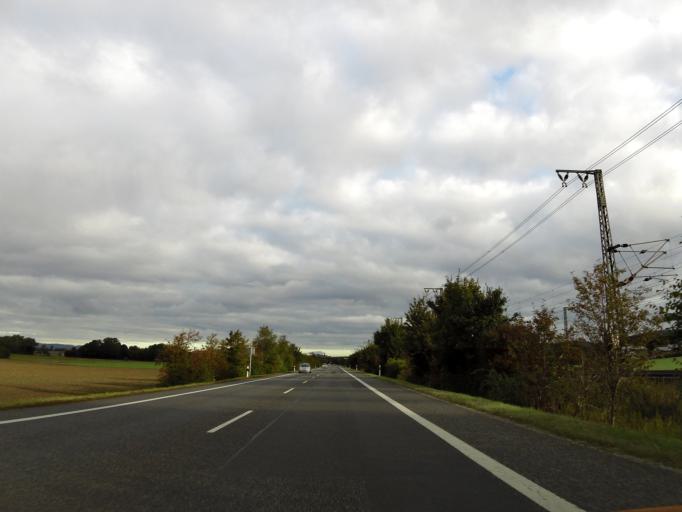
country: DE
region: Lower Saxony
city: Bovenden
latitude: 51.6097
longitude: 9.9290
